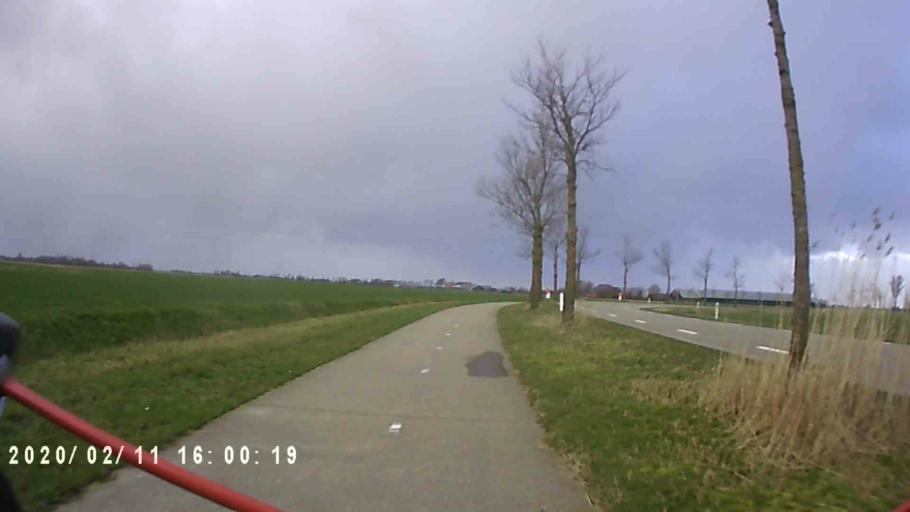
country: NL
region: Groningen
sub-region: Gemeente Zuidhorn
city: Oldehove
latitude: 53.2929
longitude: 6.4211
